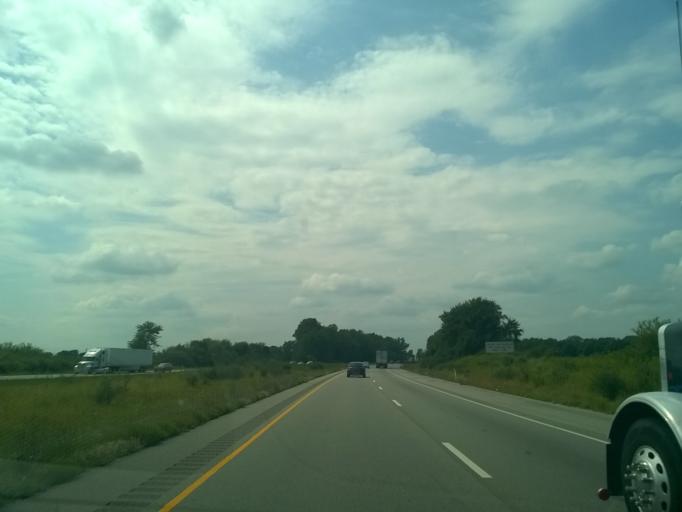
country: US
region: Indiana
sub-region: Putnam County
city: Cloverdale
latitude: 39.5616
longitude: -86.6507
